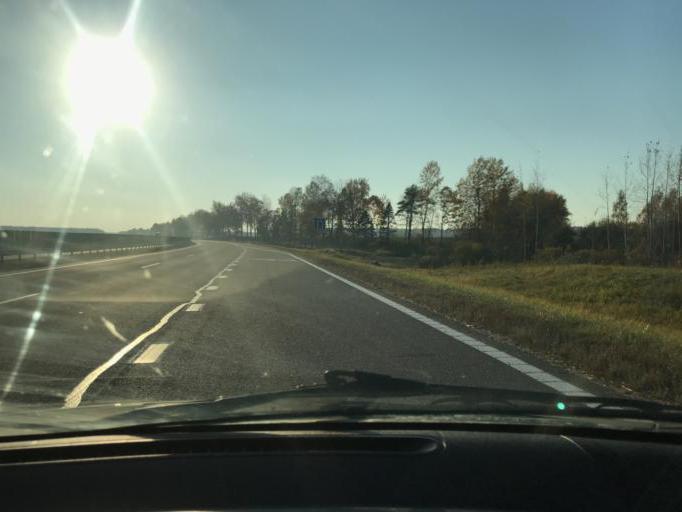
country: BY
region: Minsk
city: Loshnitsa
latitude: 54.2912
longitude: 28.7555
